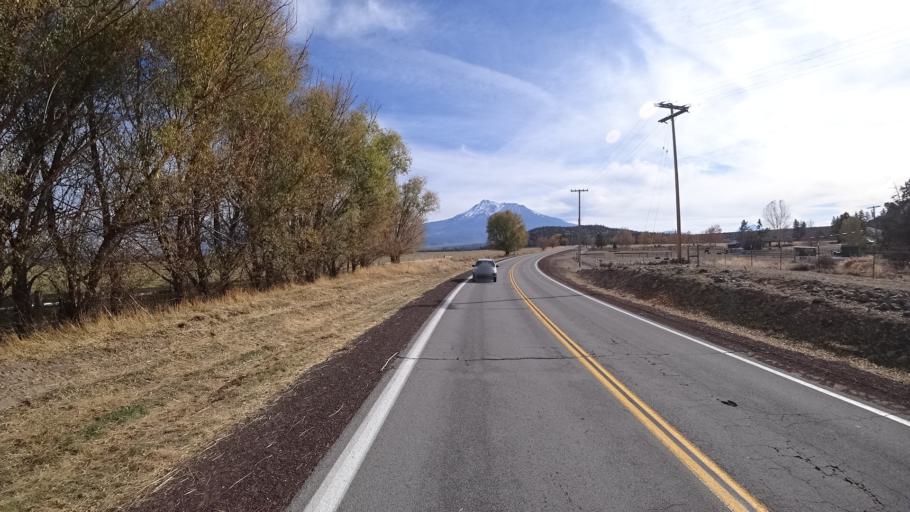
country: US
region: California
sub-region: Siskiyou County
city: Weed
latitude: 41.5485
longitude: -122.3764
